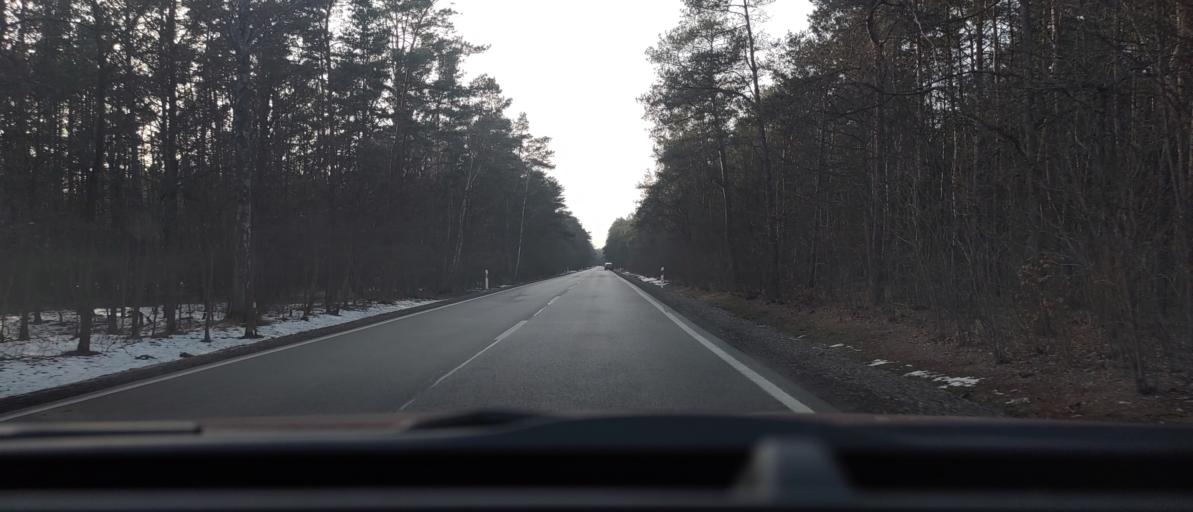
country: PL
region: Masovian Voivodeship
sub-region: Powiat bialobrzeski
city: Wysmierzyce
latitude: 51.6275
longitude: 20.8514
